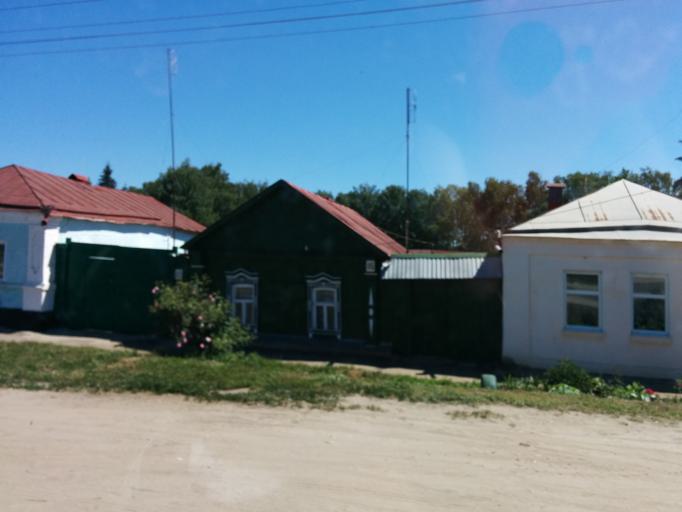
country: RU
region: Tambov
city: Morshansk
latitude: 53.4324
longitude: 41.7969
